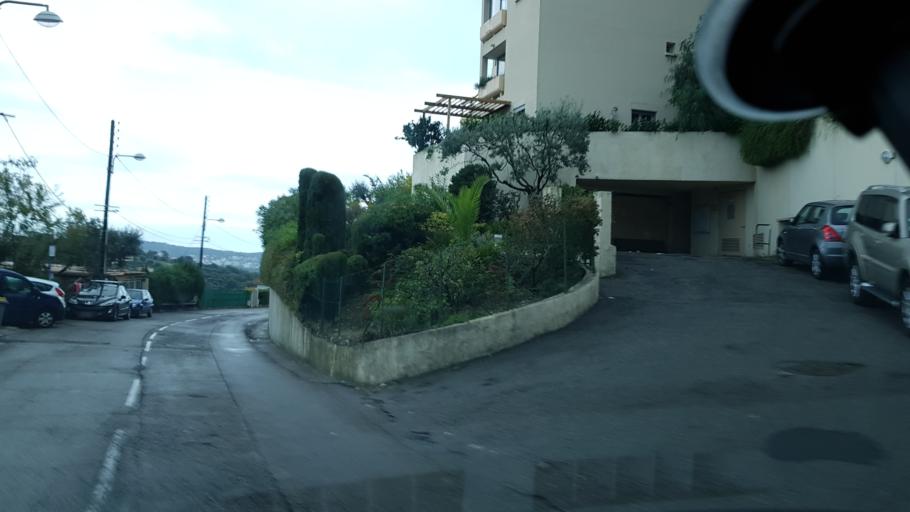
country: FR
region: Provence-Alpes-Cote d'Azur
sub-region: Departement des Alpes-Maritimes
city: Nice
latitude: 43.7021
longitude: 7.2314
